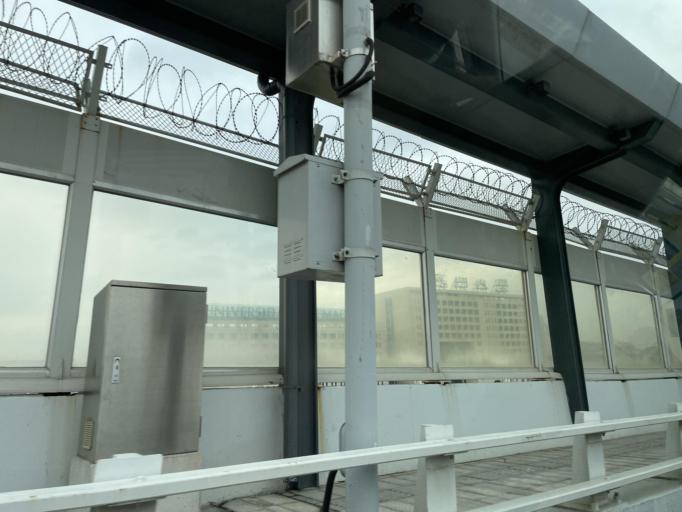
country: MO
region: Macau
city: Macau
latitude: 22.1377
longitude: 113.5463
